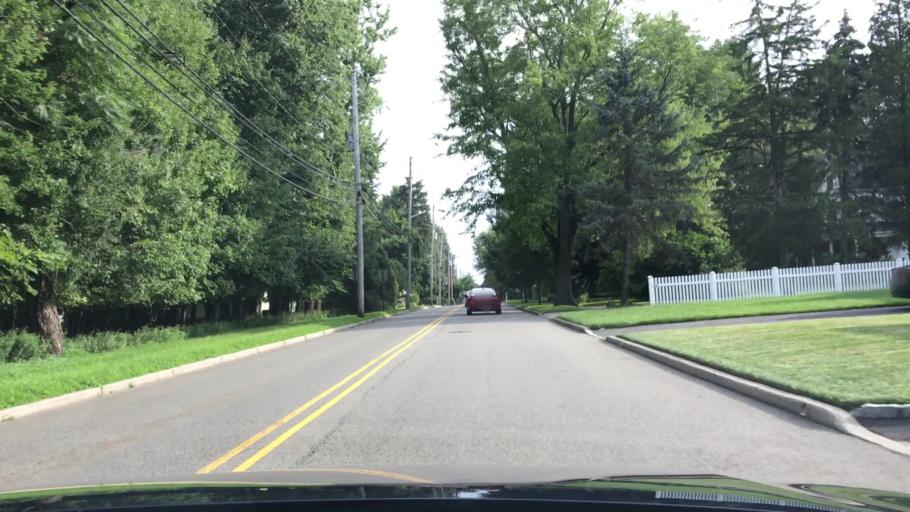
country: US
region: New Jersey
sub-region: Bergen County
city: Closter
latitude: 40.9789
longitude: -73.9588
